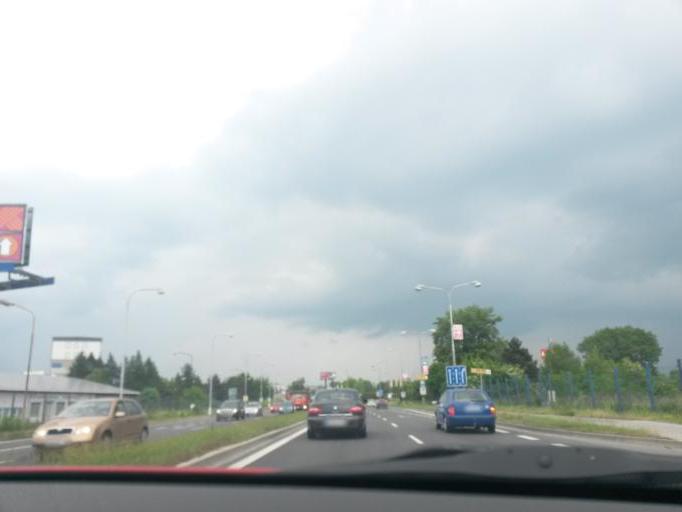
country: CZ
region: Olomoucky
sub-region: Okres Olomouc
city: Olomouc
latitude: 49.5826
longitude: 17.2656
